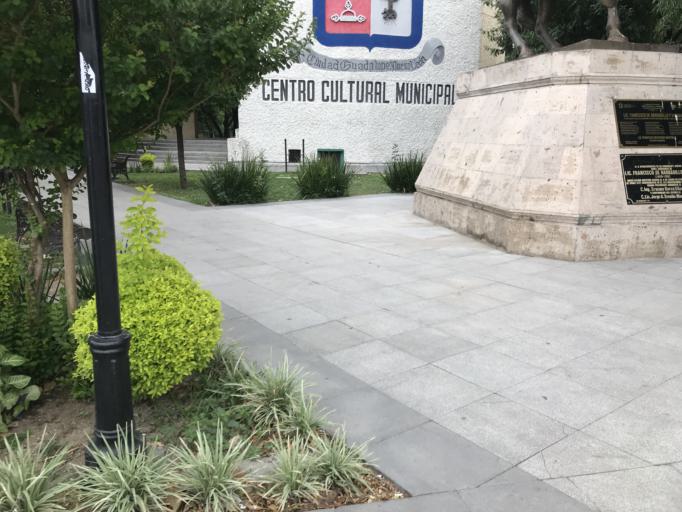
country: MX
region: Nuevo Leon
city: Guadalupe
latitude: 25.6771
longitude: -100.2595
